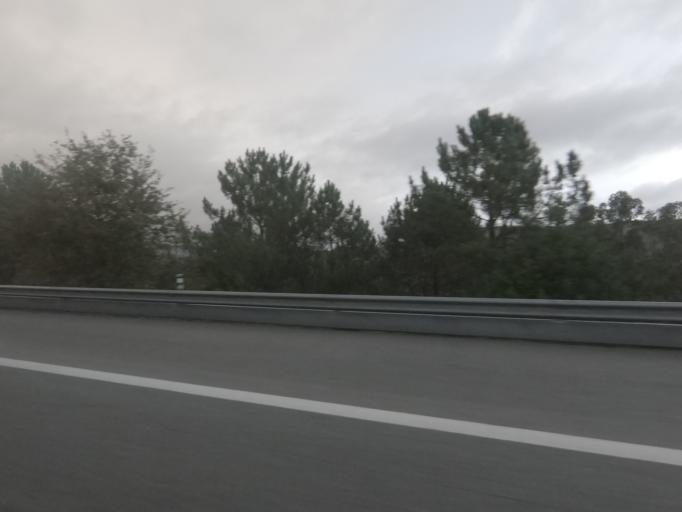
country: PT
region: Viana do Castelo
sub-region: Ponte de Lima
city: Ponte de Lima
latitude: 41.7548
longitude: -8.5572
